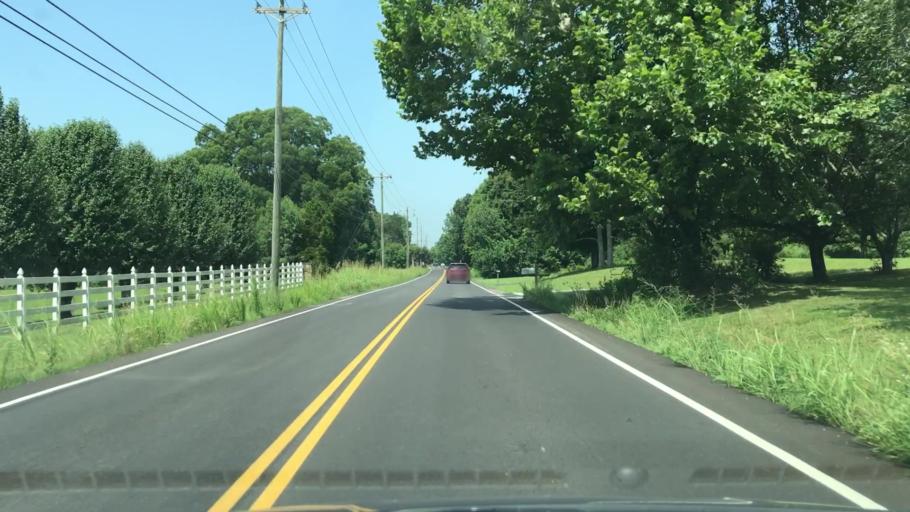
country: US
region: Tennessee
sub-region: Wilson County
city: Rural Hill
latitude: 36.1165
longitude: -86.4742
